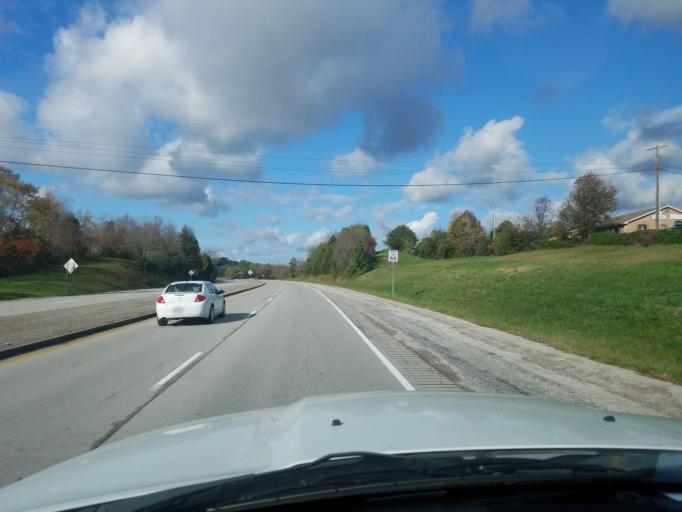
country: US
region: Kentucky
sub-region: Pulaski County
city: Somerset
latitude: 37.0936
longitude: -84.6314
